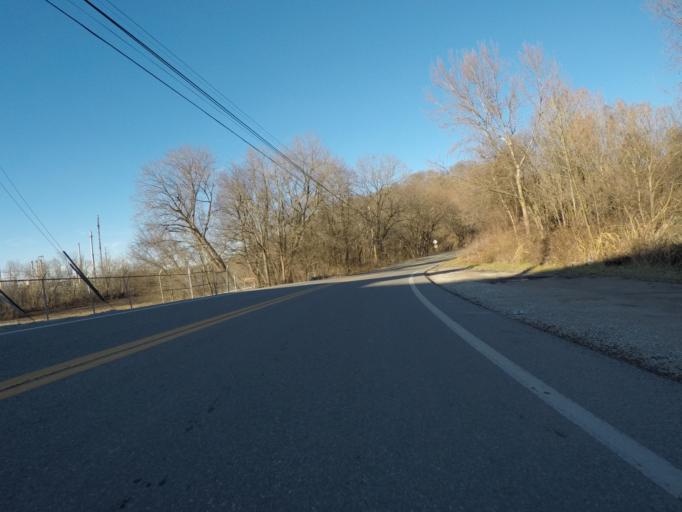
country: US
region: West Virginia
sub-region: Wayne County
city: Kenova
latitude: 38.3735
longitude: -82.5908
